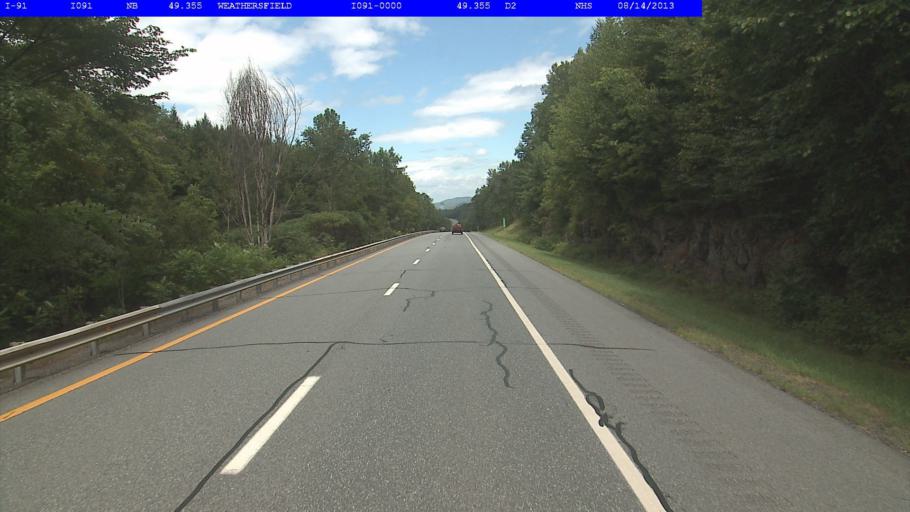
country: US
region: New Hampshire
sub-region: Sullivan County
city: Claremont
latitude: 43.3748
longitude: -72.4226
